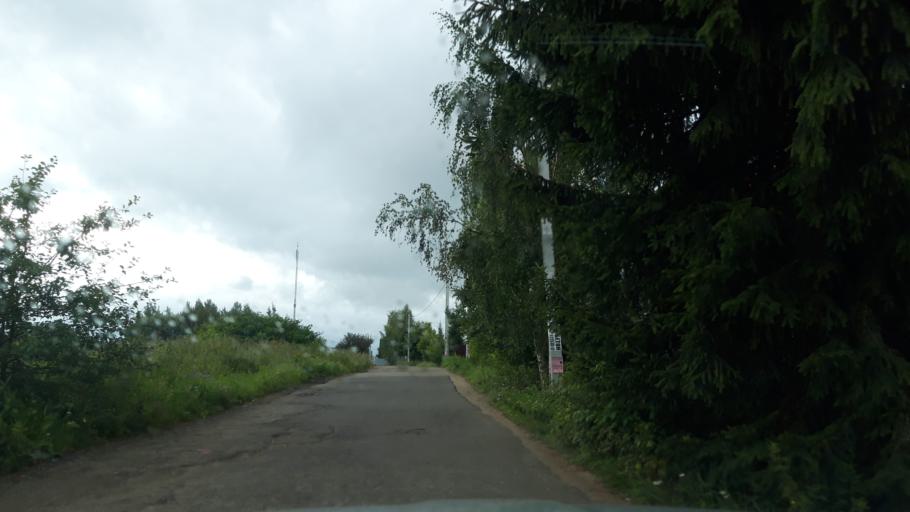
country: RU
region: Moskovskaya
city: Povarovo
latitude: 56.0960
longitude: 37.0702
